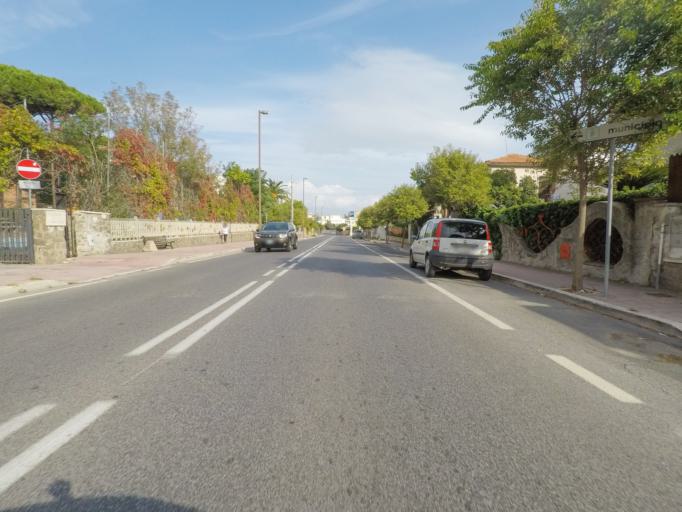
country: IT
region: Latium
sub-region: Citta metropolitana di Roma Capitale
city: Santa Marinella
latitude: 42.0336
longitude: 11.8544
